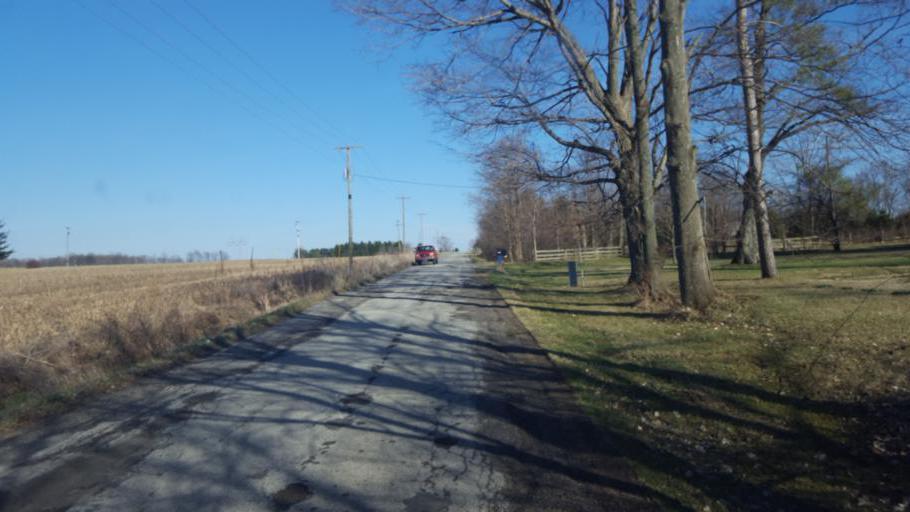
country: US
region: Ohio
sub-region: Crawford County
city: Galion
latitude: 40.6983
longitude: -82.8421
